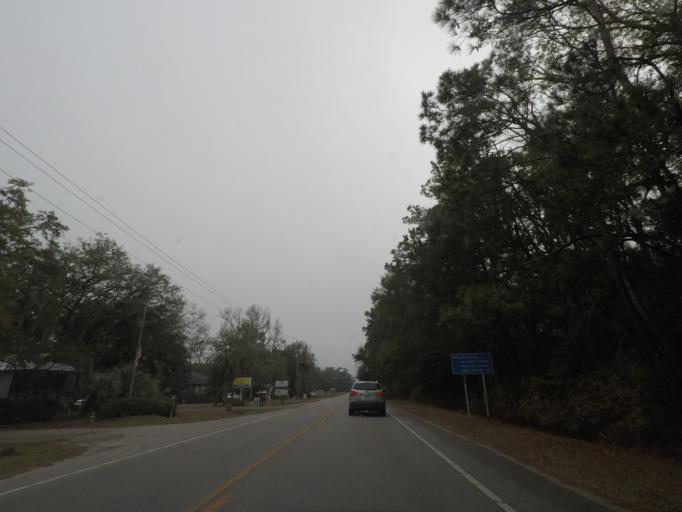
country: US
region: South Carolina
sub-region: Charleston County
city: Seabrook Island
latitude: 32.5207
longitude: -80.2999
